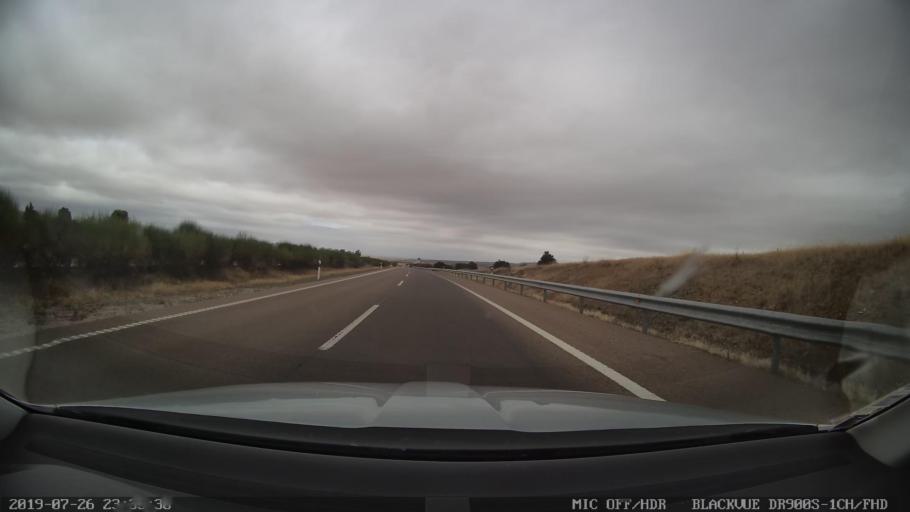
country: ES
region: Extremadura
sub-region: Provincia de Caceres
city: Santa Cruz de la Sierra
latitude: 39.3790
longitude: -5.8808
